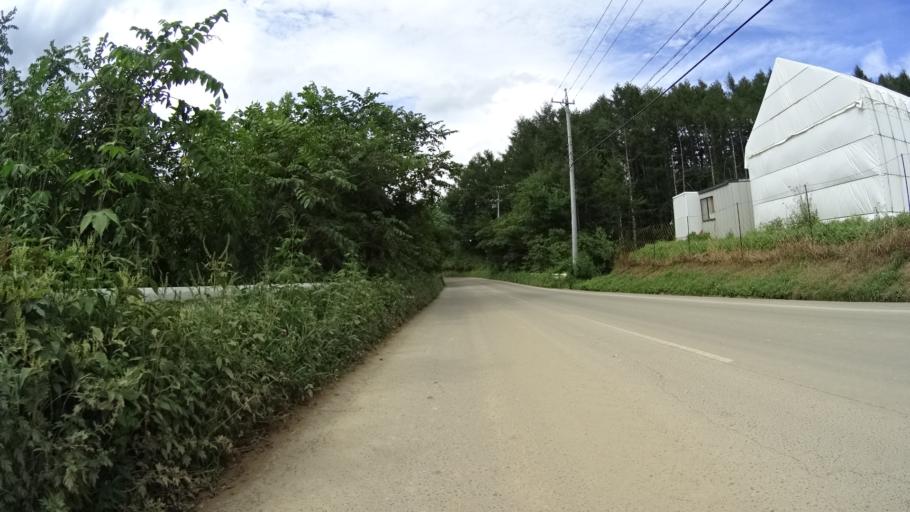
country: JP
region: Yamanashi
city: Nirasaki
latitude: 35.9494
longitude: 138.5483
